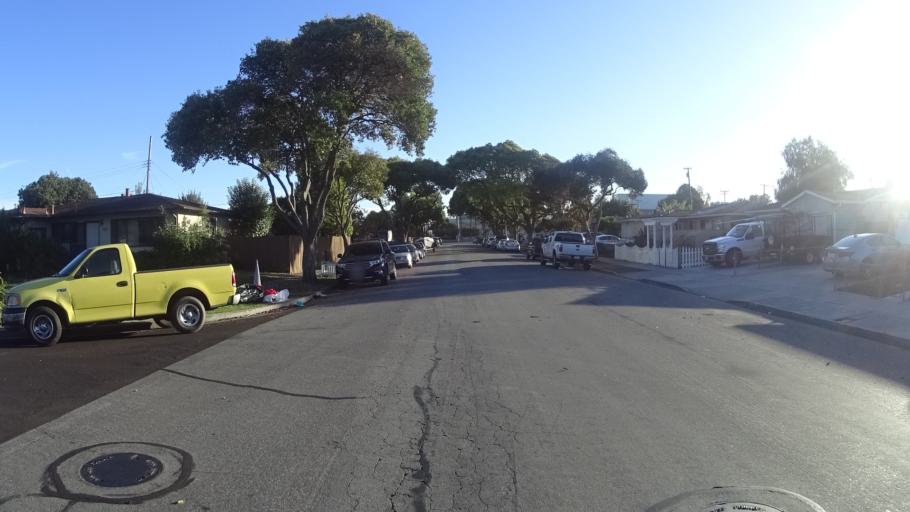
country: US
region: California
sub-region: Santa Clara County
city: Santa Clara
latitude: 37.3683
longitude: -121.9866
